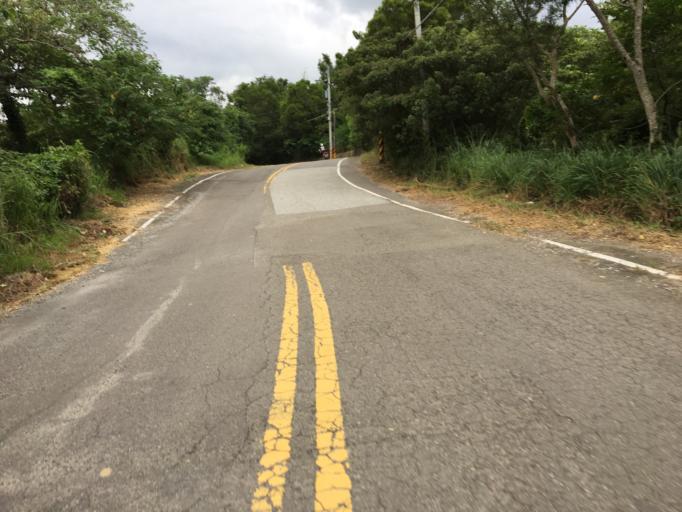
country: TW
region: Taiwan
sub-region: Hsinchu
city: Hsinchu
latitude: 24.7090
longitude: 120.9535
